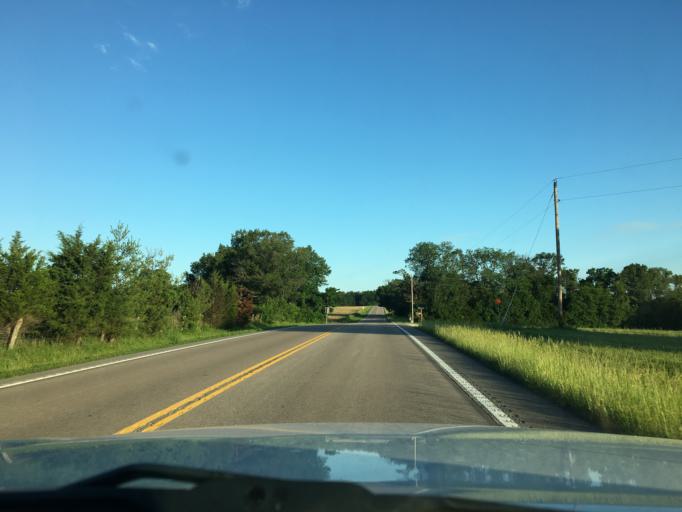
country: US
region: Missouri
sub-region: Gasconade County
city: Owensville
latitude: 38.4539
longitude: -91.4557
